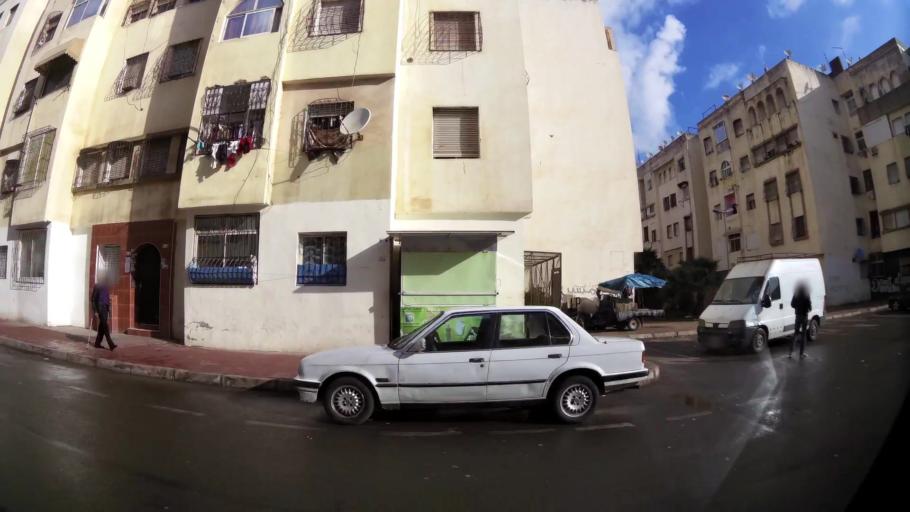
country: MA
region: Grand Casablanca
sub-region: Mediouna
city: Tit Mellil
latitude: 33.5972
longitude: -7.5337
